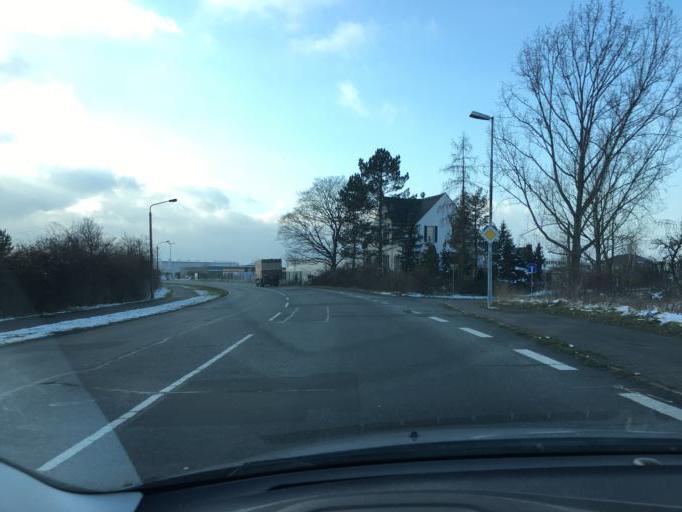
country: DE
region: Saxony
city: Brandis
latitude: 51.3547
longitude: 12.5755
